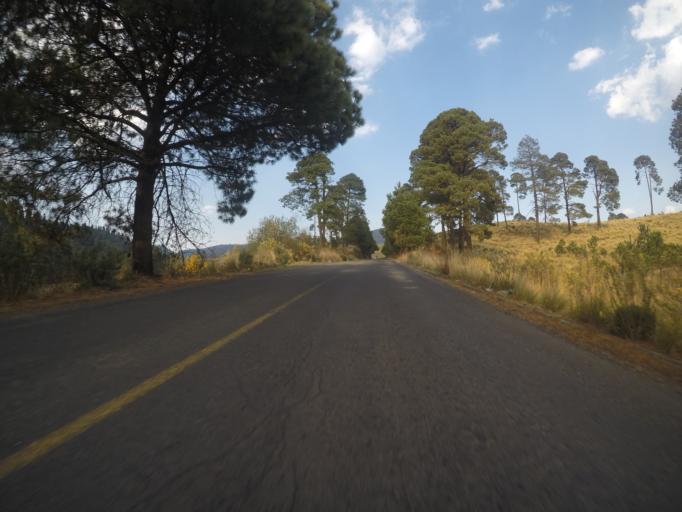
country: MX
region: Mexico
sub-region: Xalatlaco
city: San Juan Tomasquillo Herradura
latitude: 19.1837
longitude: -99.3545
